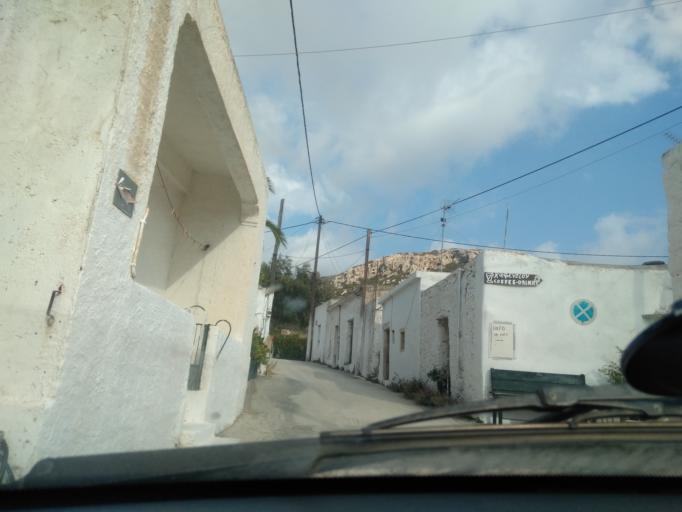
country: GR
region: Crete
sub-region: Nomos Lasithiou
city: Makry-Gialos
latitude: 35.0454
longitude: 26.0596
